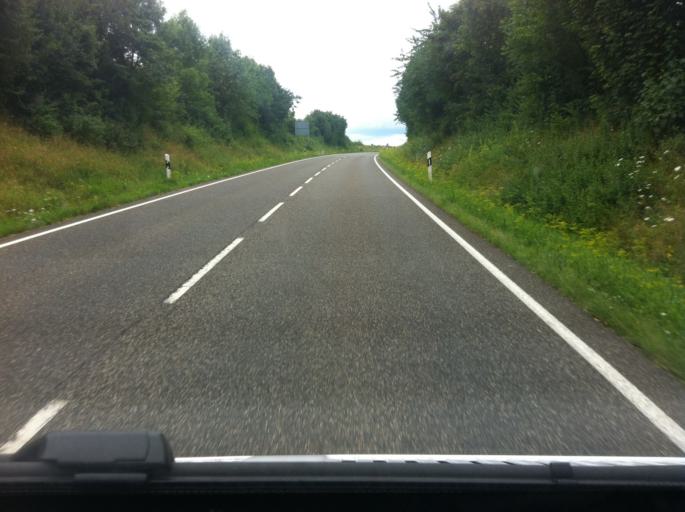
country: DE
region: North Rhine-Westphalia
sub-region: Regierungsbezirk Koln
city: Nettersheim
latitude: 50.4928
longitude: 6.6191
